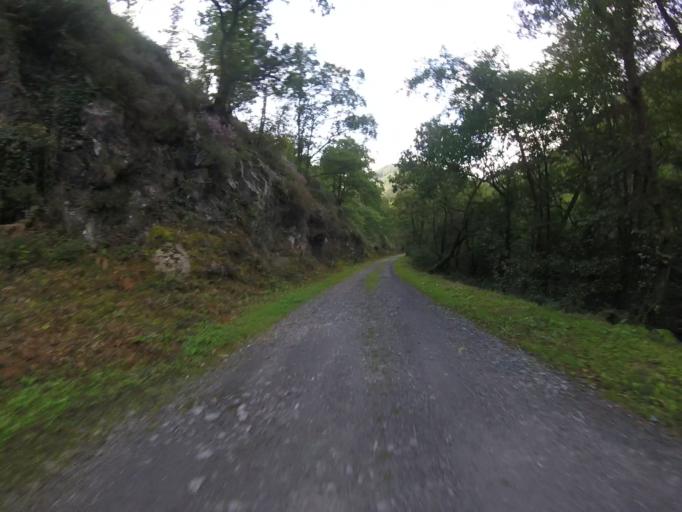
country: ES
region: Basque Country
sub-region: Provincia de Guipuzcoa
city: Berastegui
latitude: 43.1524
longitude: -1.9642
